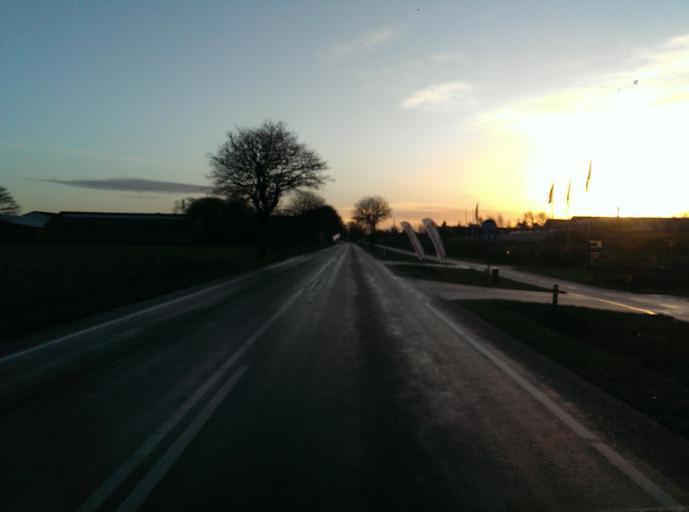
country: DK
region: South Denmark
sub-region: Esbjerg Kommune
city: Bramming
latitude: 55.4695
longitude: 8.6718
